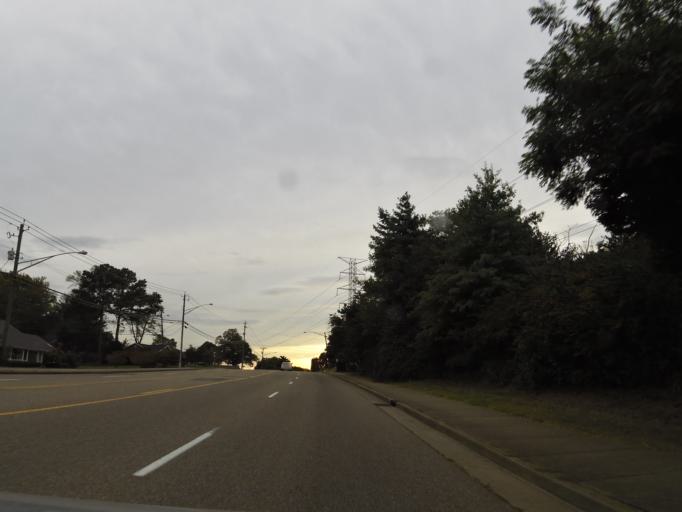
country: US
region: Tennessee
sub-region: Blount County
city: Louisville
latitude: 35.9218
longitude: -84.0385
